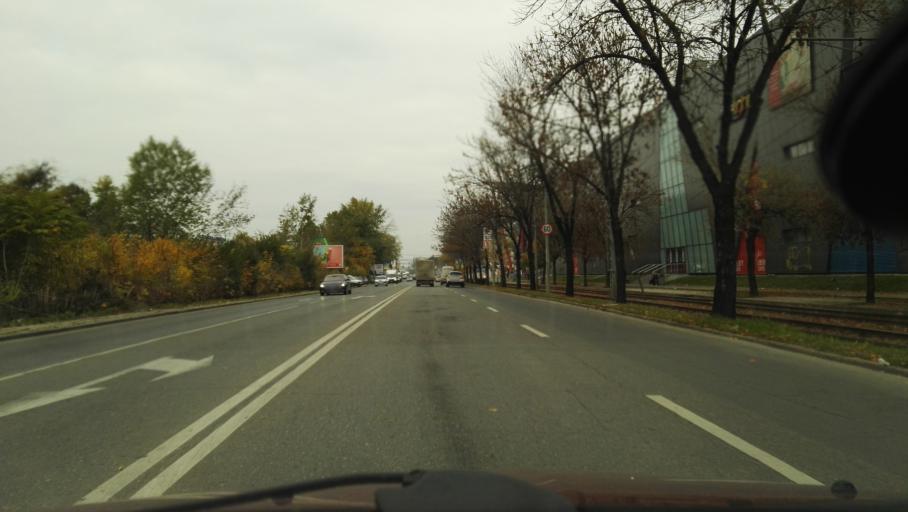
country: RO
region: Bucuresti
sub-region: Municipiul Bucuresti
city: Bucuresti
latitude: 44.4140
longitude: 26.0804
